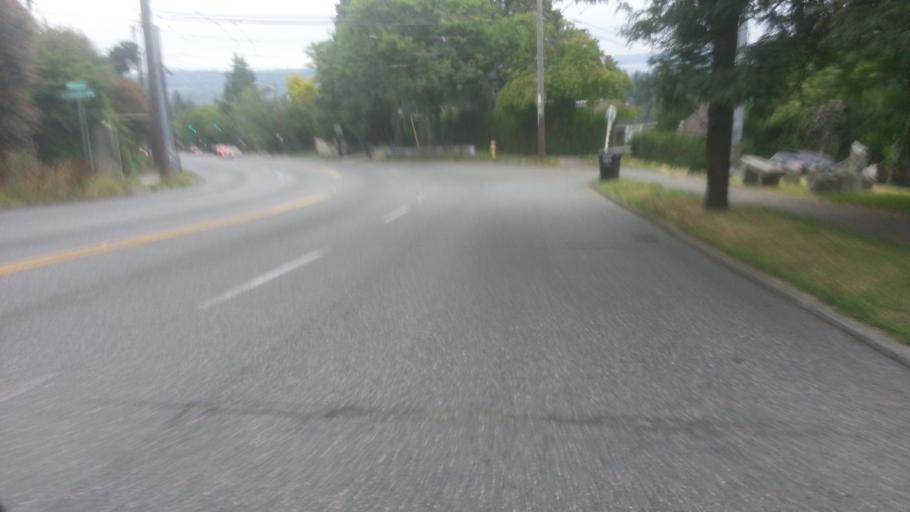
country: US
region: Washington
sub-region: King County
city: Seattle
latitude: 47.6279
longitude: -122.3018
